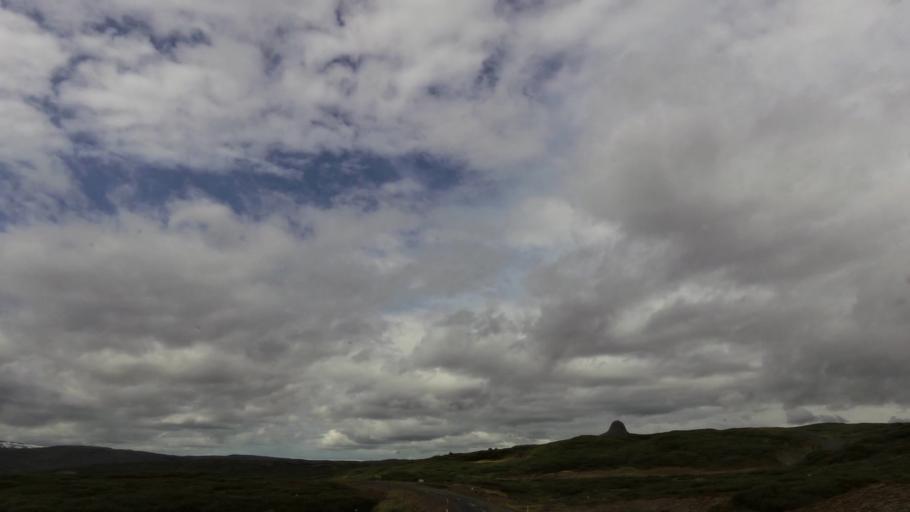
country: IS
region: West
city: Stykkisholmur
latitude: 65.5438
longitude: -22.0957
